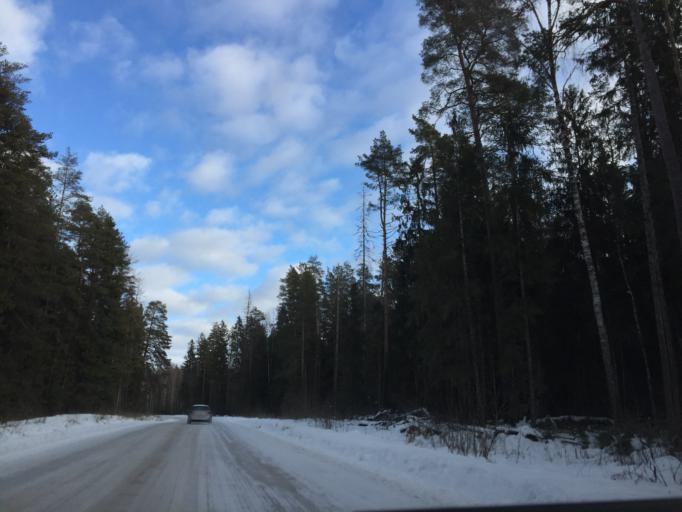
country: LV
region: Ogre
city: Jumprava
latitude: 56.5818
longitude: 24.9543
